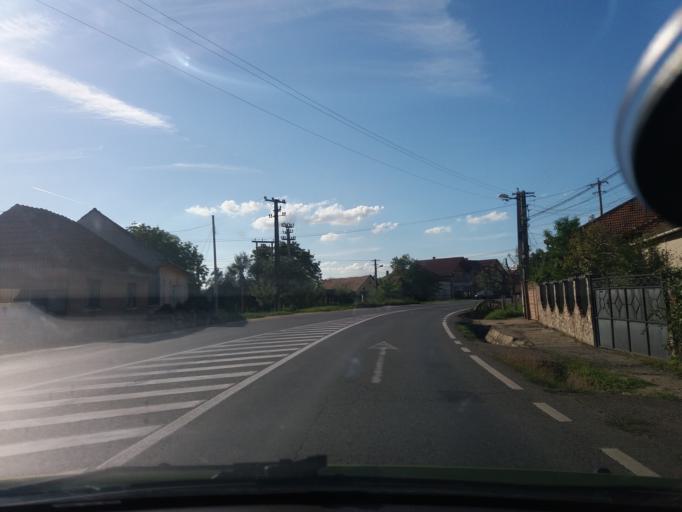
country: RO
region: Arad
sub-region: Oras Lipova
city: Radna
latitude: 46.0934
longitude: 21.6827
